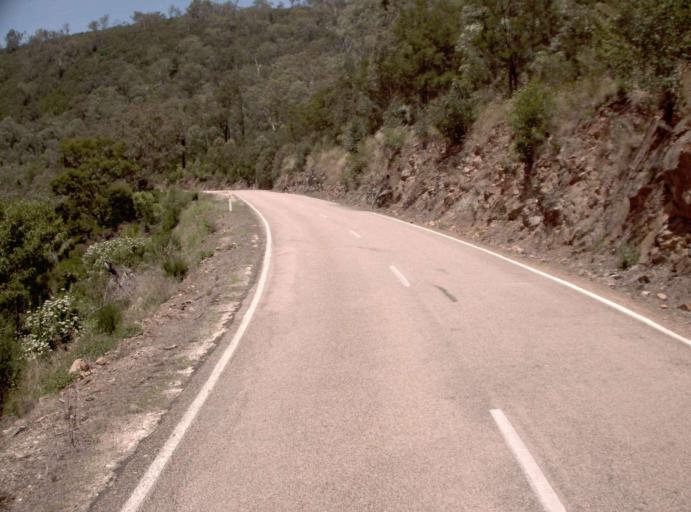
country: AU
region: Victoria
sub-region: East Gippsland
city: Lakes Entrance
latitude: -37.5329
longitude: 147.8538
